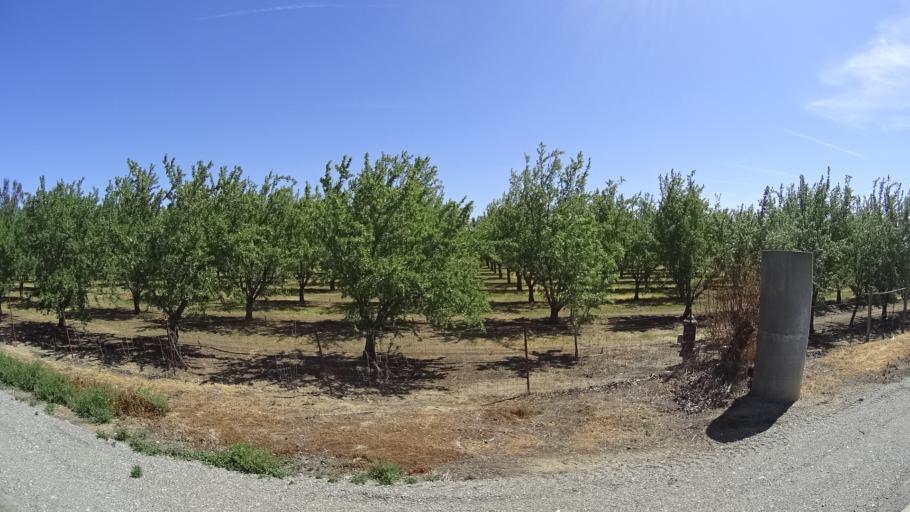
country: US
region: California
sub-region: Glenn County
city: Orland
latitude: 39.7006
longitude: -122.1780
